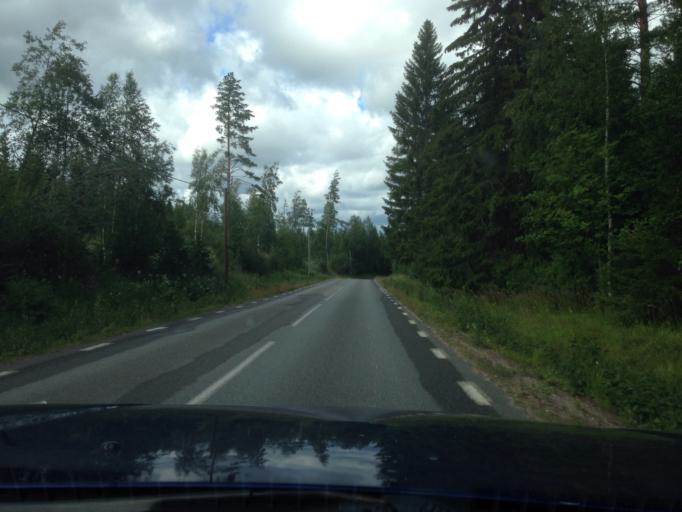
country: SE
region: Dalarna
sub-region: Vansbro Kommun
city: Jarna
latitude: 60.3901
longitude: 14.4891
